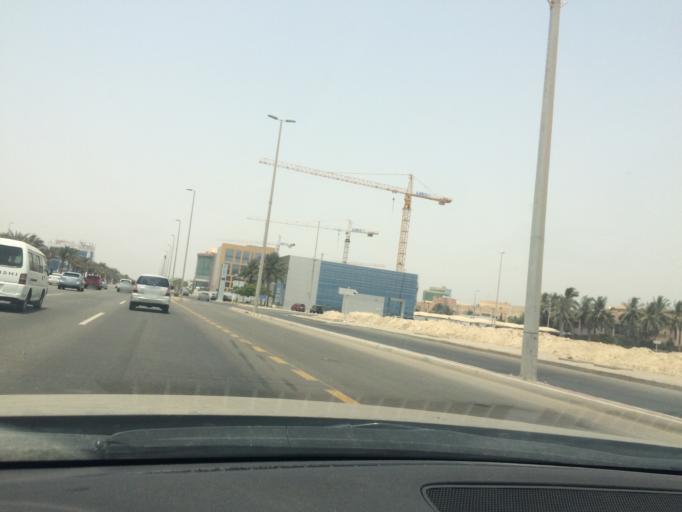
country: SA
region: Makkah
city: Jeddah
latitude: 21.6426
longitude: 39.1118
